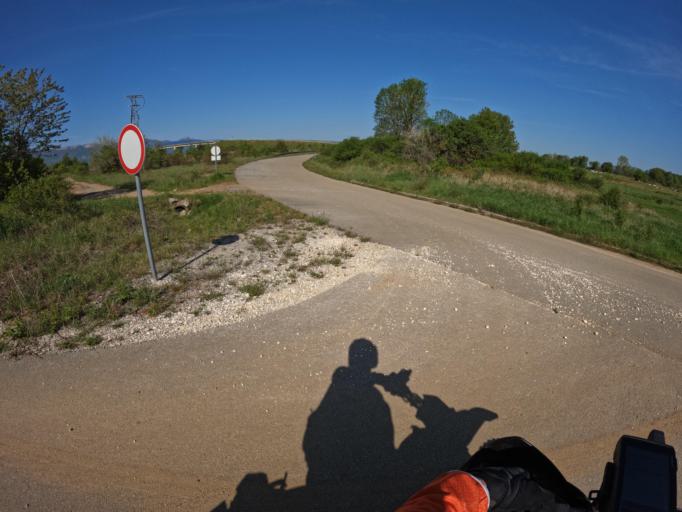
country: HR
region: Licko-Senjska
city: Gospic
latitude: 44.4808
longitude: 15.5652
